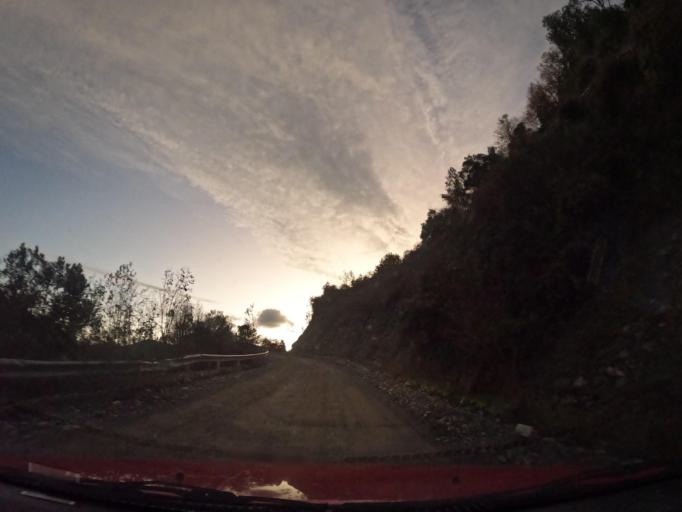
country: CL
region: Maule
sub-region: Provincia de Linares
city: Colbun
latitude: -35.8574
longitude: -71.2226
